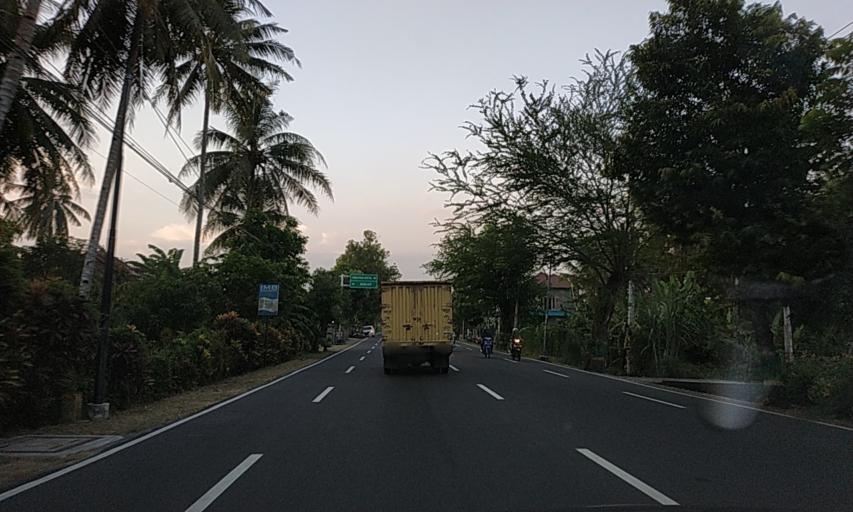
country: ID
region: Daerah Istimewa Yogyakarta
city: Srandakan
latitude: -7.8795
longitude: 110.1324
